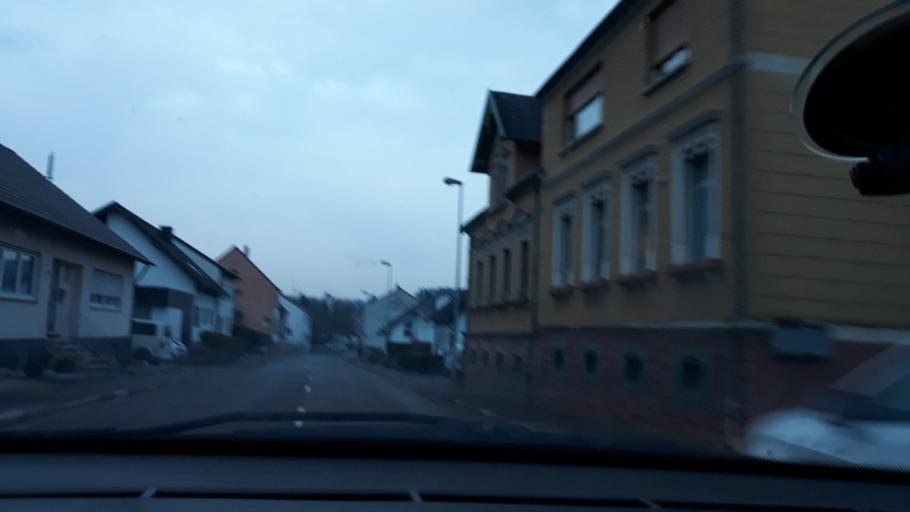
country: DE
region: Saarland
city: Sankt Ingbert
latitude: 49.2657
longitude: 7.1573
